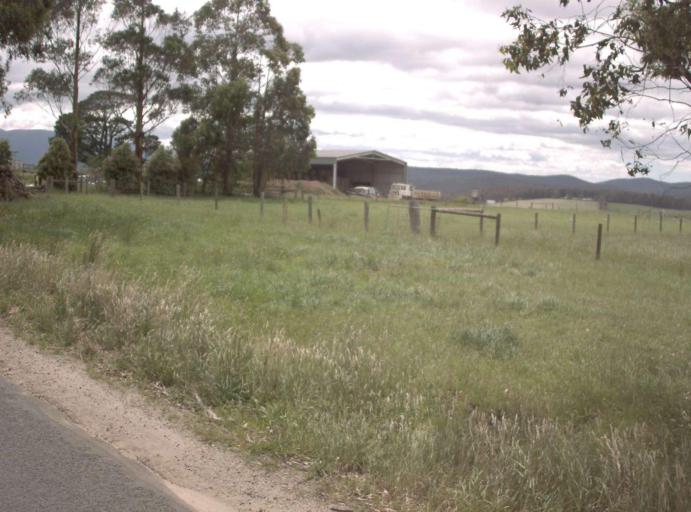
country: AU
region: Victoria
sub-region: Latrobe
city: Moe
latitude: -37.9984
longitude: 146.1455
